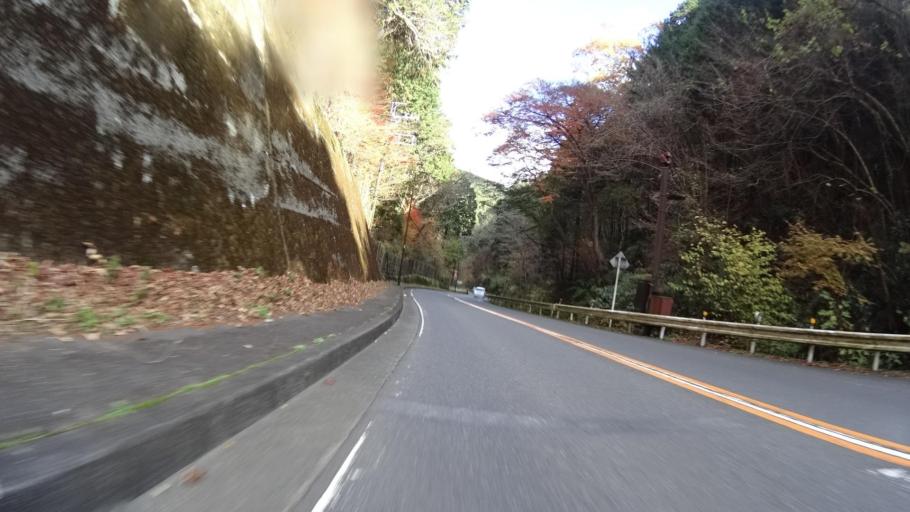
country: JP
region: Tokyo
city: Hachioji
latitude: 35.6192
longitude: 139.2327
